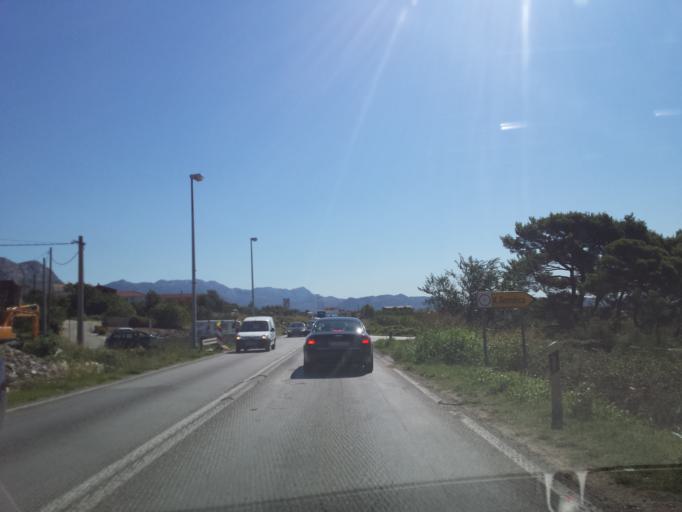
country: HR
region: Splitsko-Dalmatinska
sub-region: Grad Split
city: Split
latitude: 43.5539
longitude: 16.4023
